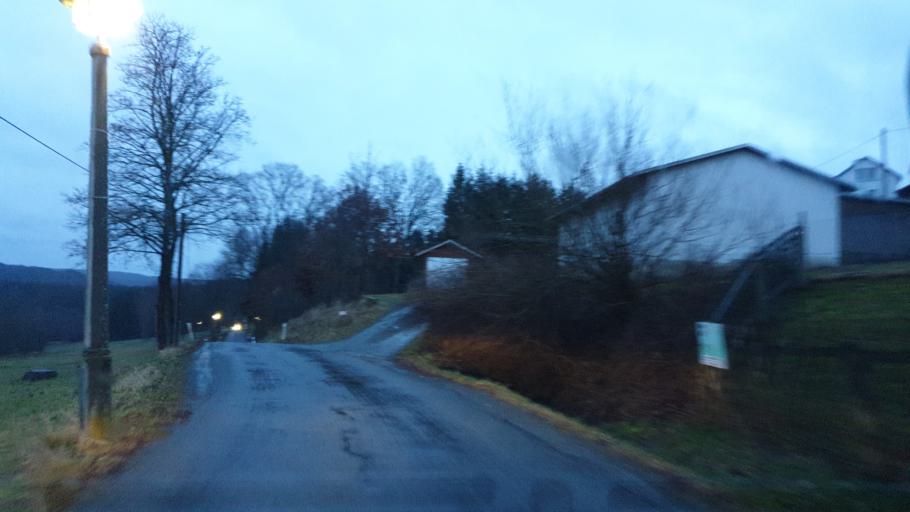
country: DE
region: Saxony
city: Bad Elster
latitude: 50.3079
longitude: 12.2331
